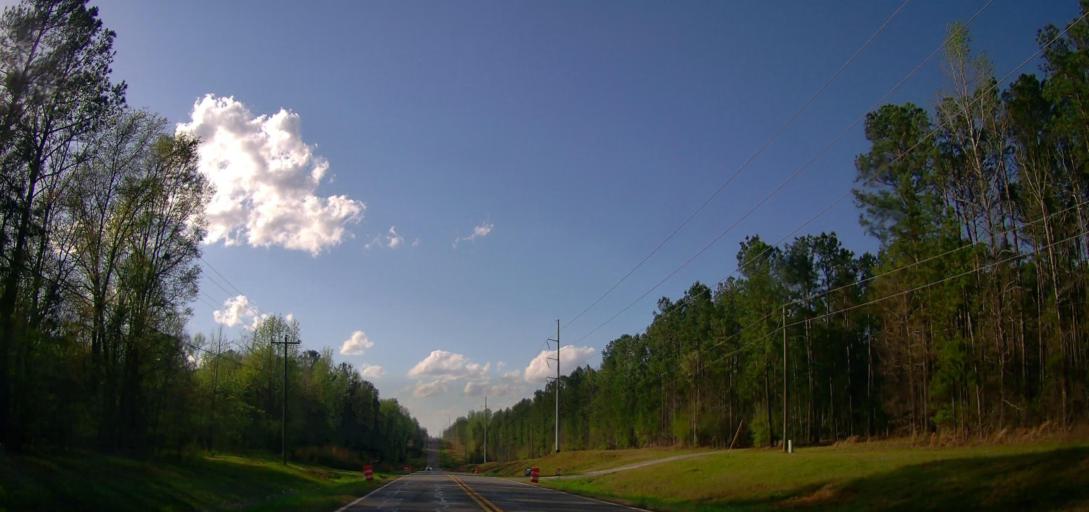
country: US
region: Georgia
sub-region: Baldwin County
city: Milledgeville
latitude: 33.1324
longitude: -83.3217
